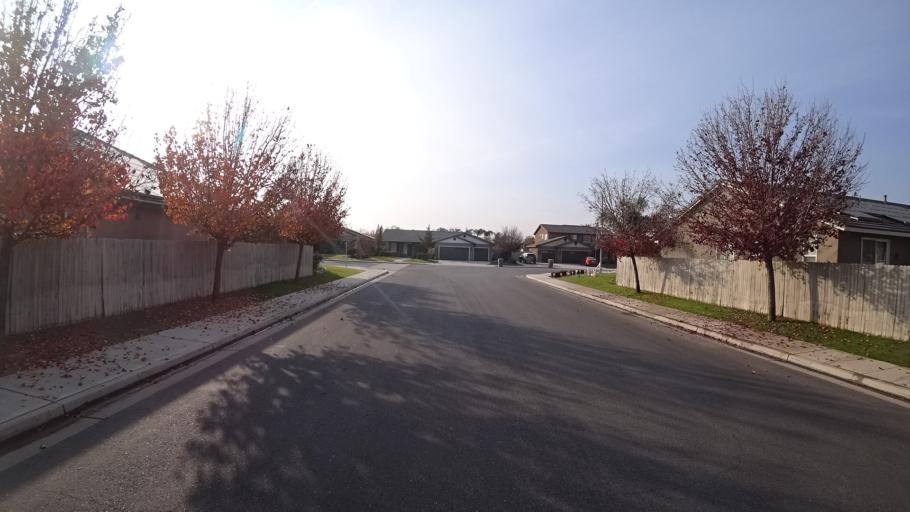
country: US
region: California
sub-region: Kern County
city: Greenacres
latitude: 35.4352
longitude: -119.1161
